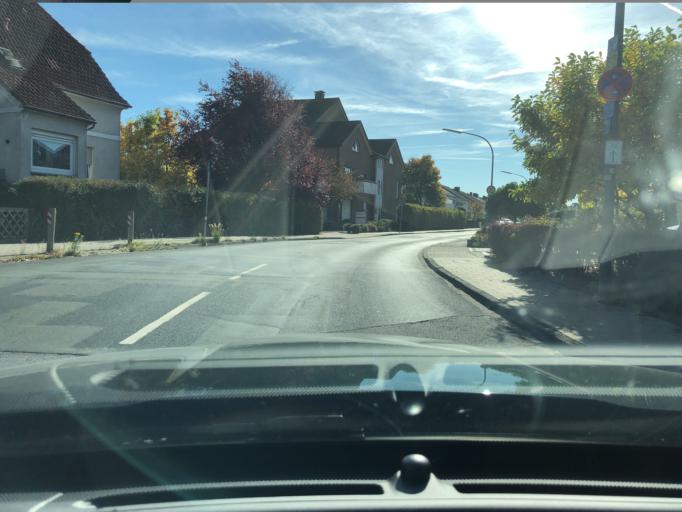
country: DE
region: Lower Saxony
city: Hasbergen
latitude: 52.2589
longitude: 7.9882
